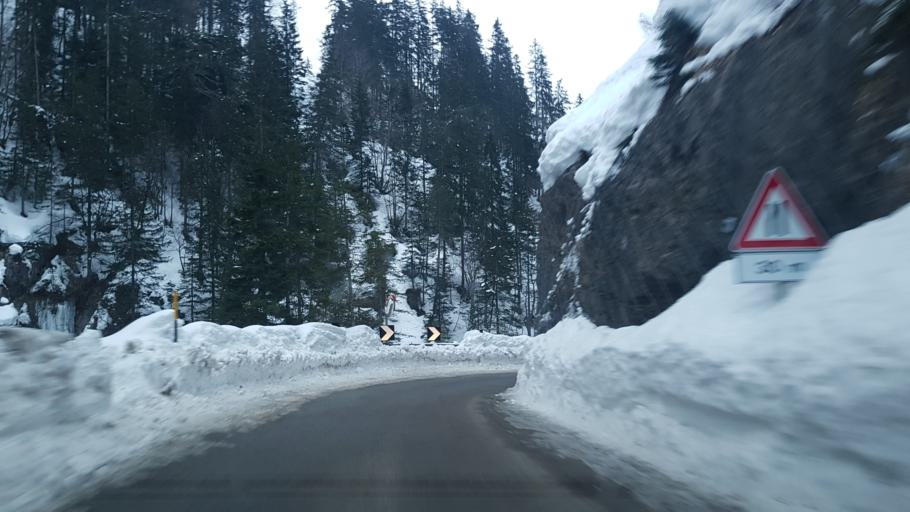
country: IT
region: Friuli Venezia Giulia
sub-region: Provincia di Udine
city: Malborghetto
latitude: 46.5254
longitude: 13.4739
